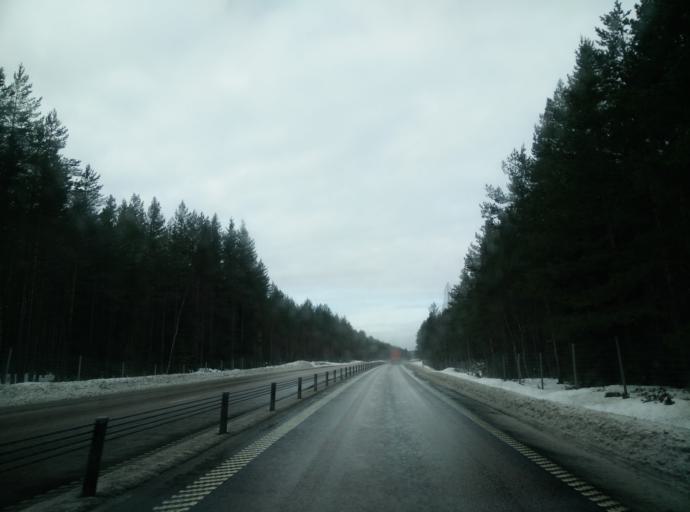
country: SE
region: Dalarna
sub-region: Hedemora Kommun
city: Langshyttan
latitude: 60.5547
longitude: 16.0820
